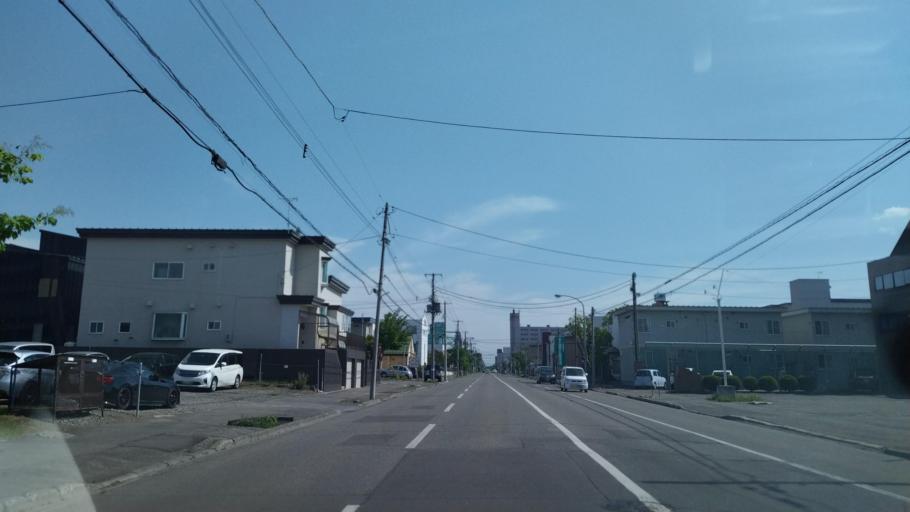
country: JP
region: Hokkaido
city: Obihiro
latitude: 42.9287
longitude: 143.2077
